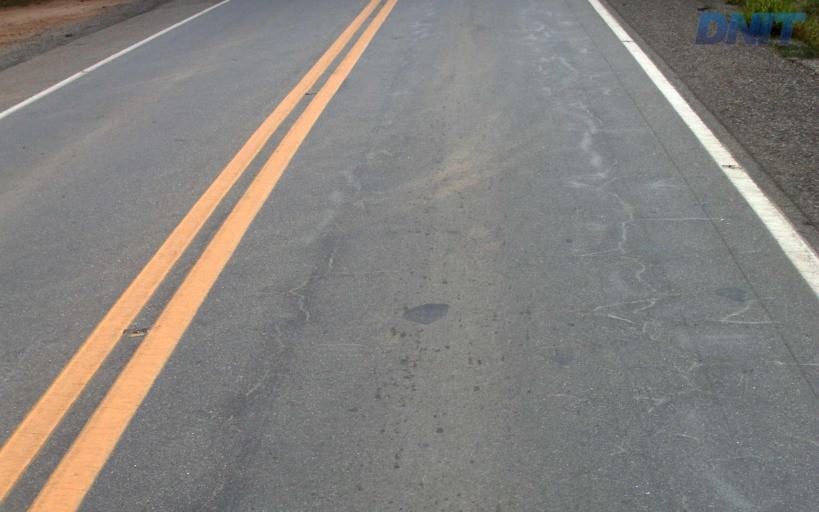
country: BR
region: Minas Gerais
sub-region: Governador Valadares
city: Governador Valadares
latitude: -19.0224
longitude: -42.1448
